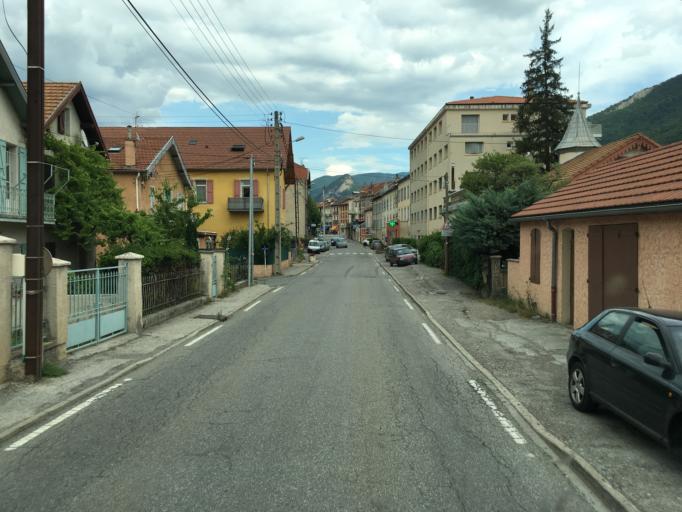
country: FR
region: Provence-Alpes-Cote d'Azur
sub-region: Departement des Hautes-Alpes
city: Veynes
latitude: 44.5331
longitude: 5.8183
